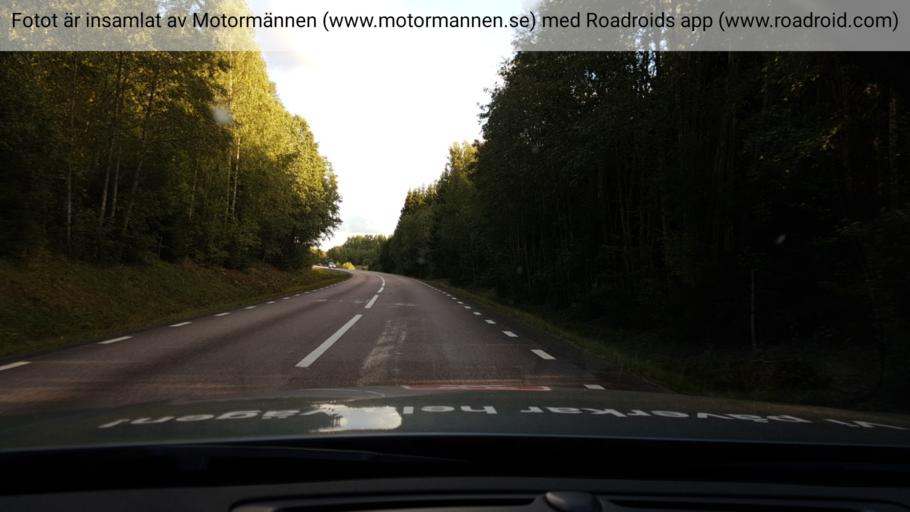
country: SE
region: Vaermland
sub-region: Karlstads Kommun
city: Molkom
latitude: 59.6493
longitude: 13.7119
